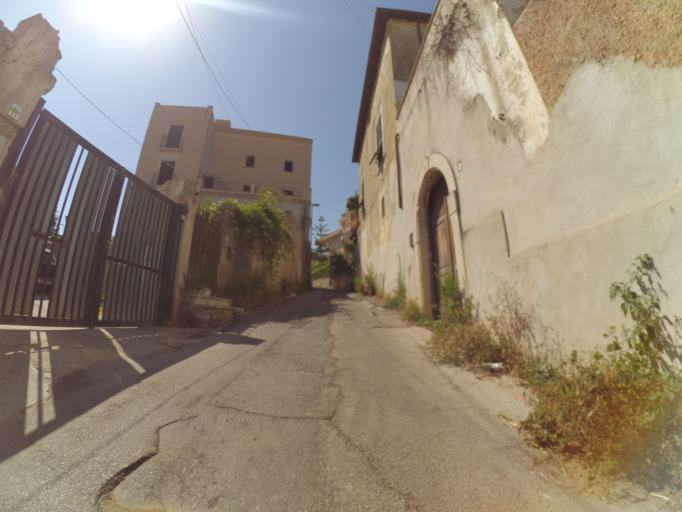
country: IT
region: Latium
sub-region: Provincia di Latina
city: Gaeta
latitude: 41.2181
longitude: 13.5580
